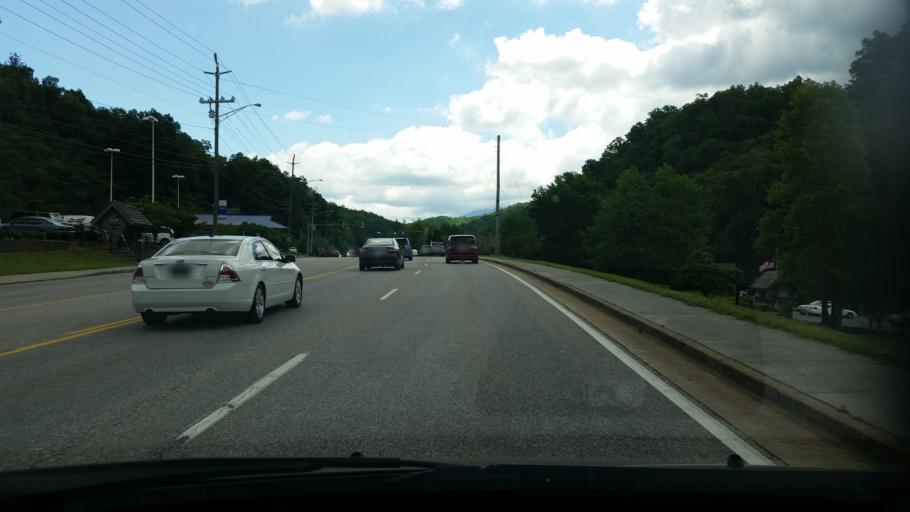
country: US
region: Tennessee
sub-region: Sevier County
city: Gatlinburg
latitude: 35.7260
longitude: -83.4814
